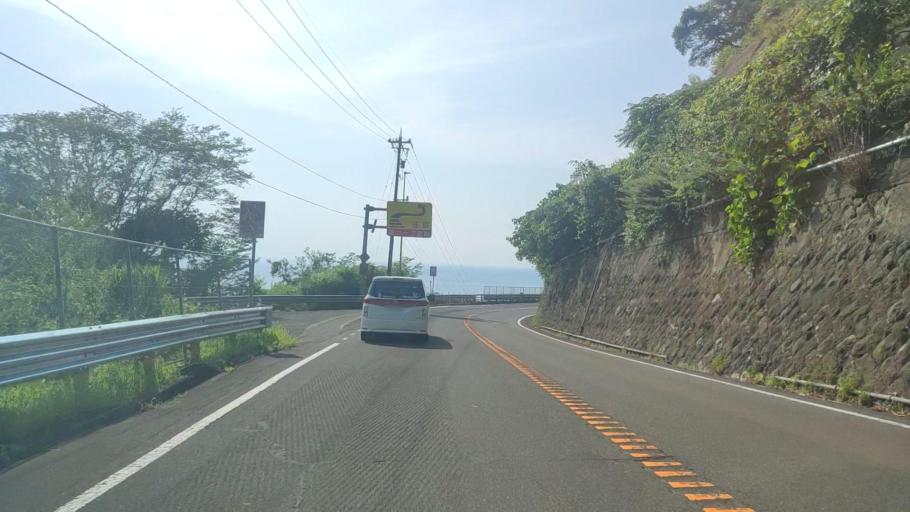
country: JP
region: Fukui
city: Tsuruga
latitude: 35.7748
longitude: 136.1049
